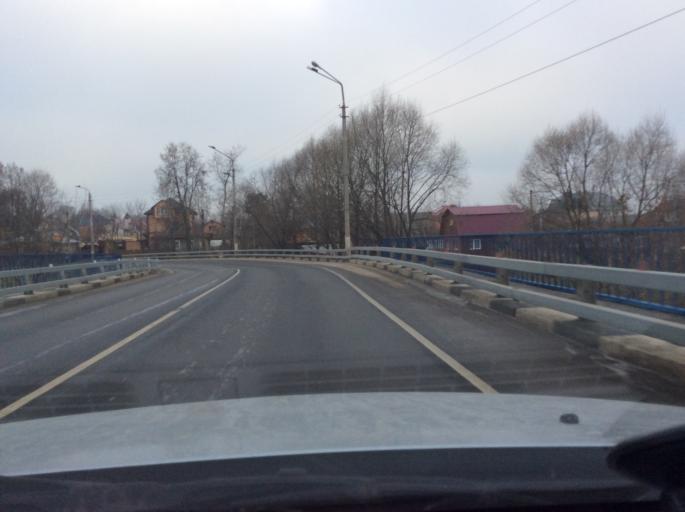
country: RU
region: Moskovskaya
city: Filimonki
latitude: 55.5258
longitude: 37.3812
